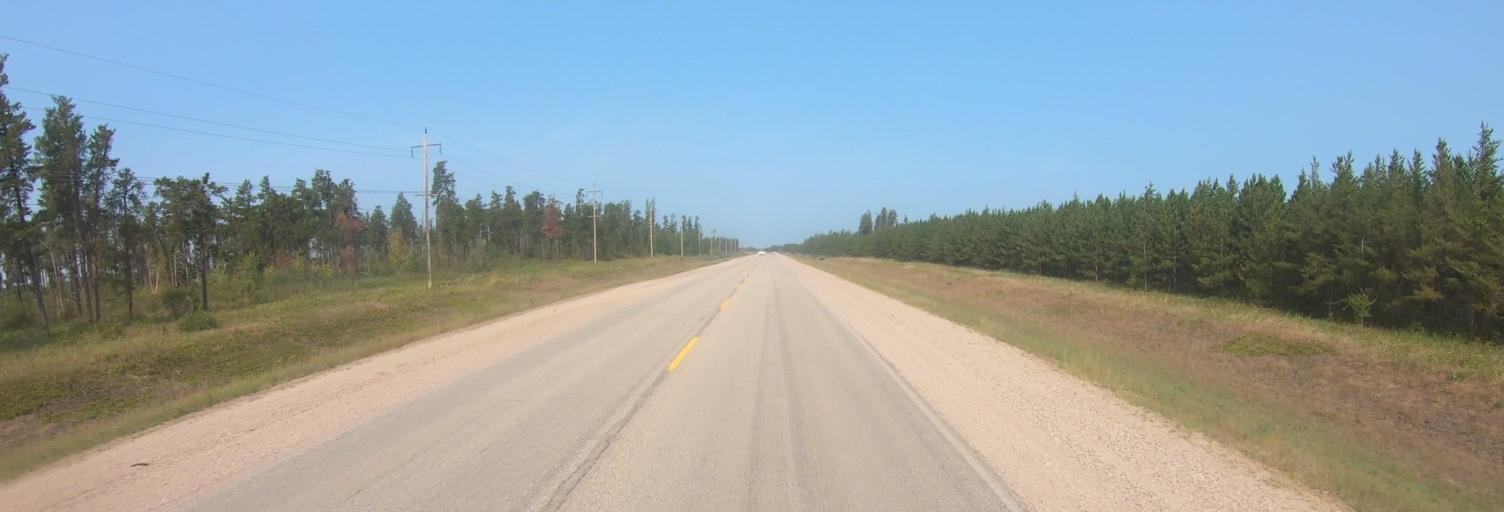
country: US
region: Minnesota
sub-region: Roseau County
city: Roseau
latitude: 49.0835
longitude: -95.8767
